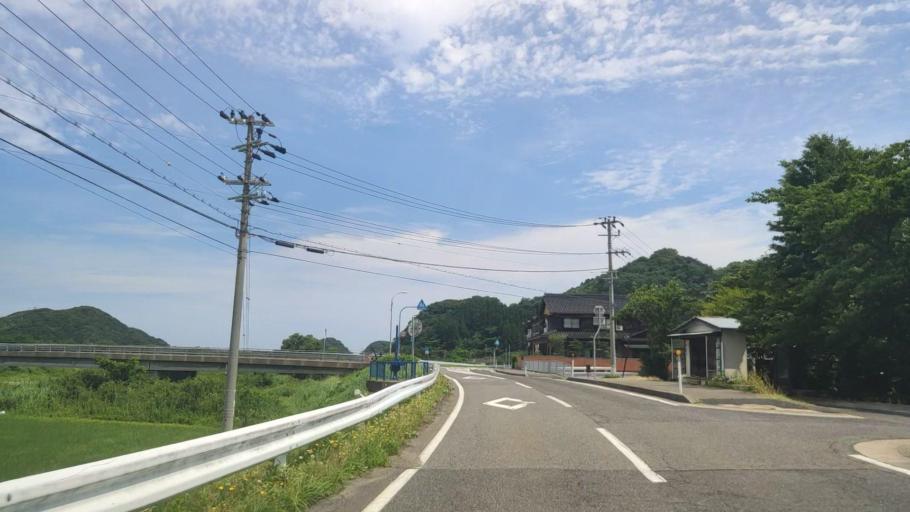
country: JP
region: Hyogo
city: Toyooka
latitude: 35.6477
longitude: 134.7637
